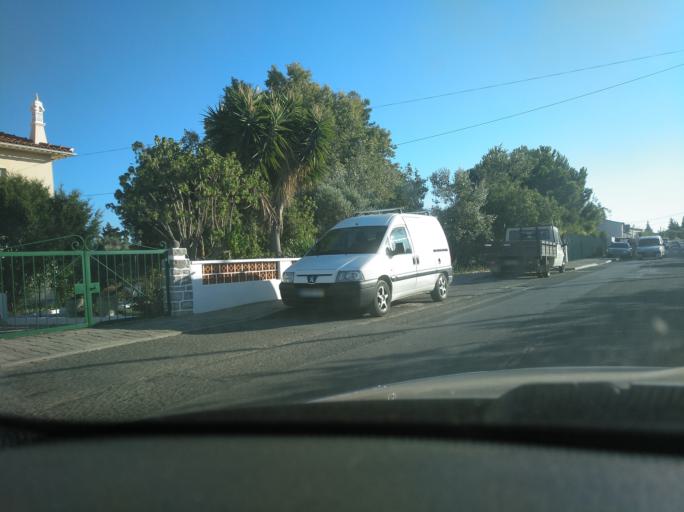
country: PT
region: Faro
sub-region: Vila Real de Santo Antonio
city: Monte Gordo
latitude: 37.1717
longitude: -7.5374
